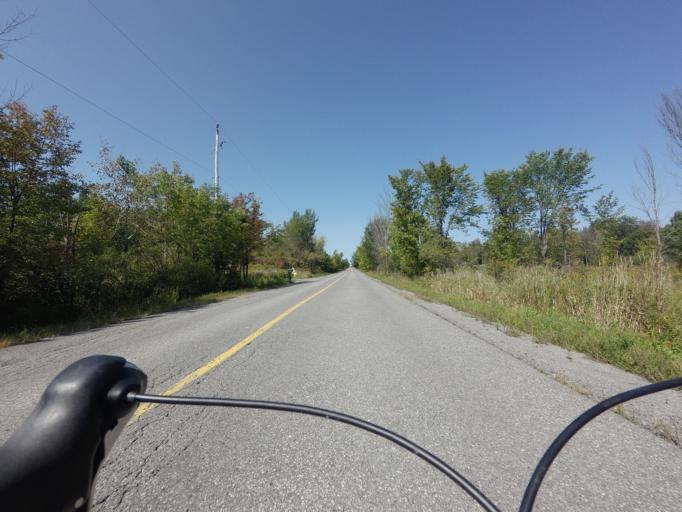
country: CA
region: Ontario
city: Bells Corners
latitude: 45.3923
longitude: -76.0308
